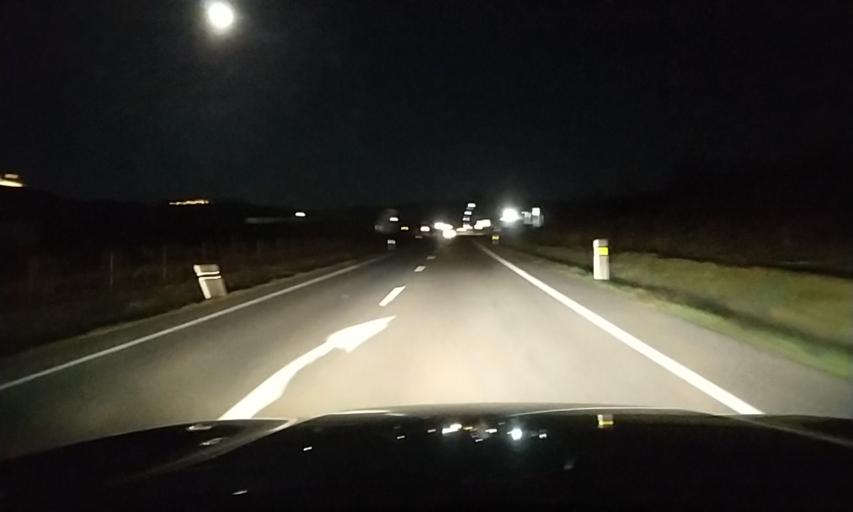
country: ES
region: Galicia
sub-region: Provincia de Ourense
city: Verin
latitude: 41.9425
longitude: -7.4679
